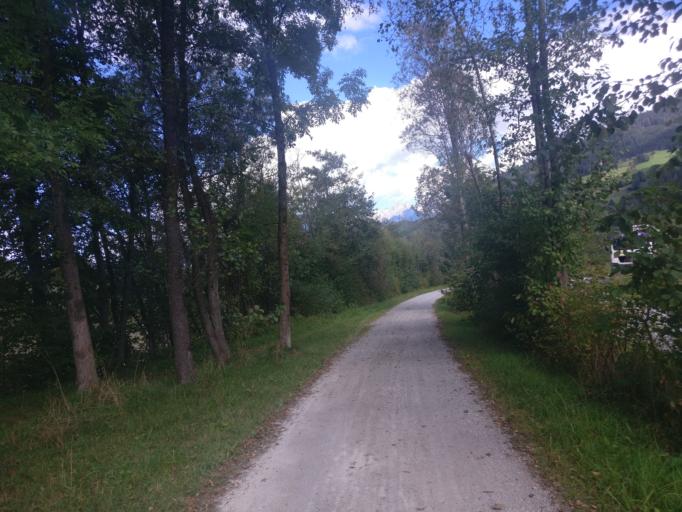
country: AT
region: Salzburg
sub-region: Politischer Bezirk Sankt Johann im Pongau
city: Bischofshofen
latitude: 47.3933
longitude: 13.2196
